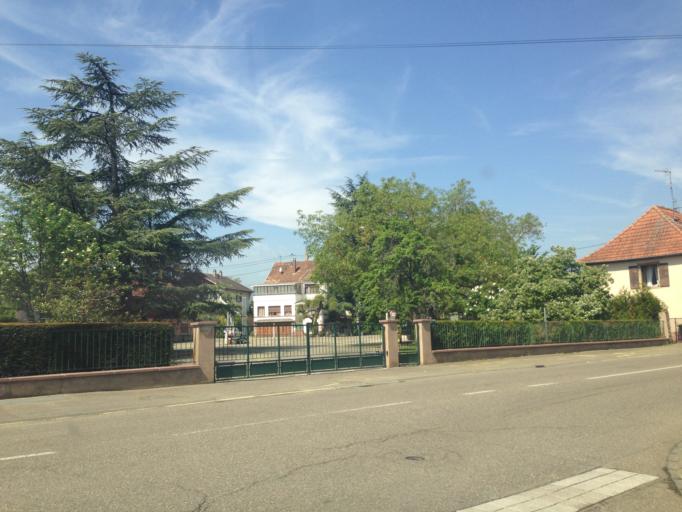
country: FR
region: Alsace
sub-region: Departement du Bas-Rhin
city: Obernai
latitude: 48.4581
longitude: 7.4837
